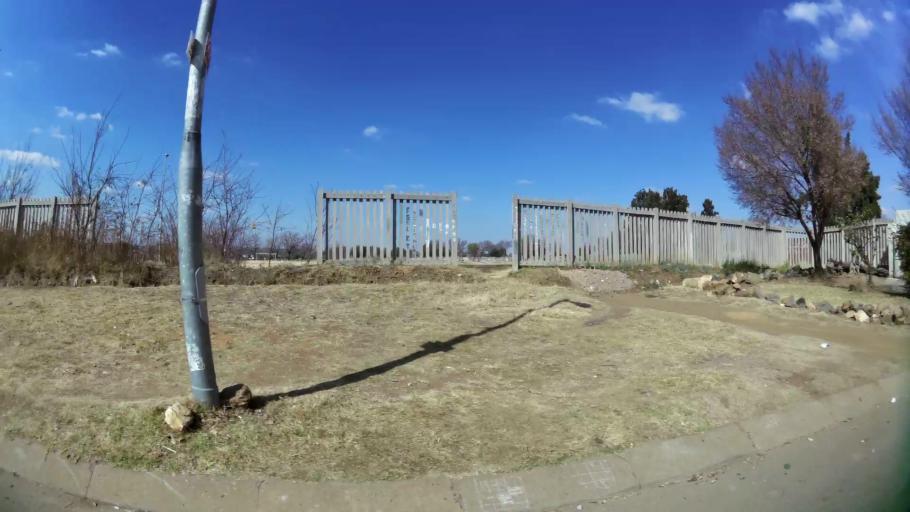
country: ZA
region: Gauteng
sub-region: City of Johannesburg Metropolitan Municipality
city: Soweto
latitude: -26.2486
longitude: 27.8876
